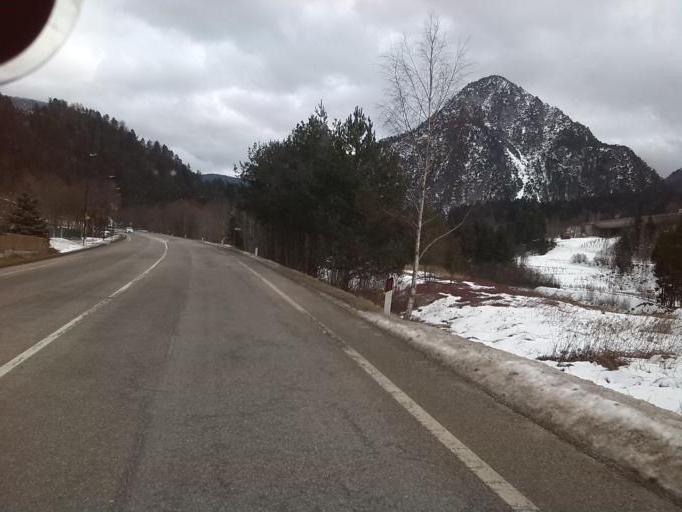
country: IT
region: Friuli Venezia Giulia
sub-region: Provincia di Udine
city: Malborghetto
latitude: 46.5063
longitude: 13.4456
